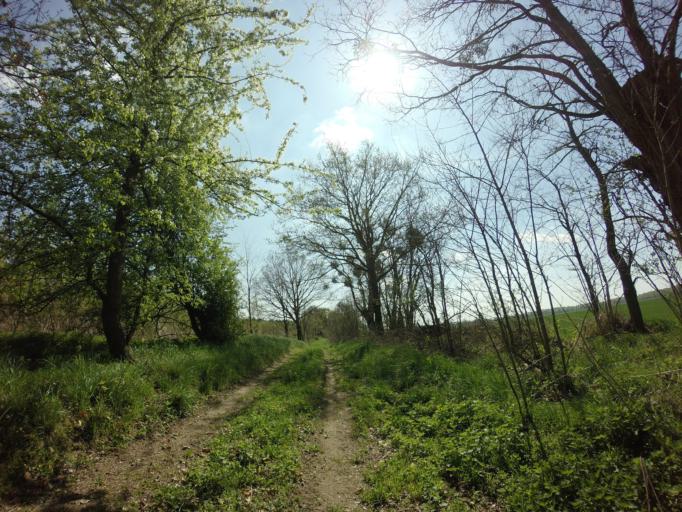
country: PL
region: West Pomeranian Voivodeship
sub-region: Powiat stargardzki
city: Suchan
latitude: 53.2105
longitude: 15.3038
